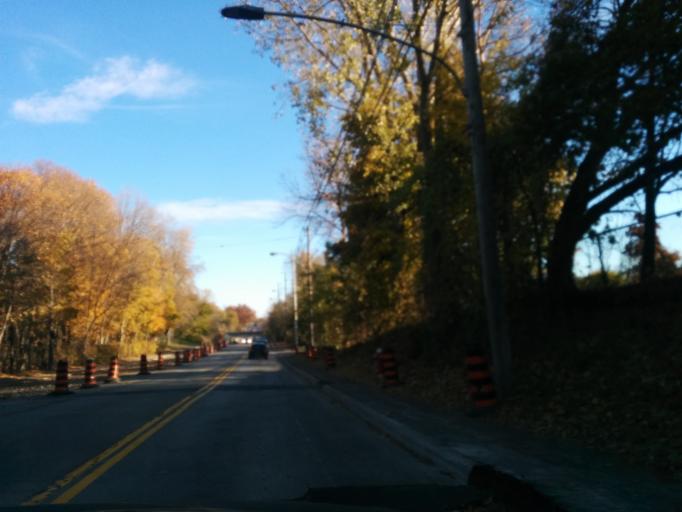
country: CA
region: Ontario
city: Etobicoke
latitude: 43.5884
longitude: -79.5568
